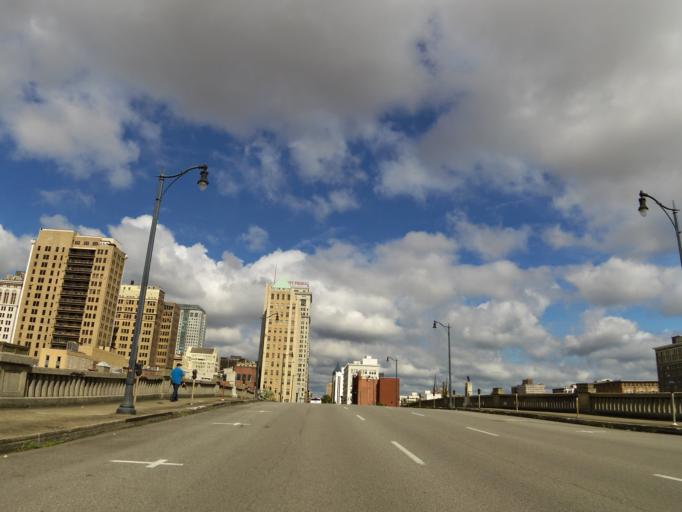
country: US
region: Alabama
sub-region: Jefferson County
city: Birmingham
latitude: 33.5133
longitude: -86.8030
